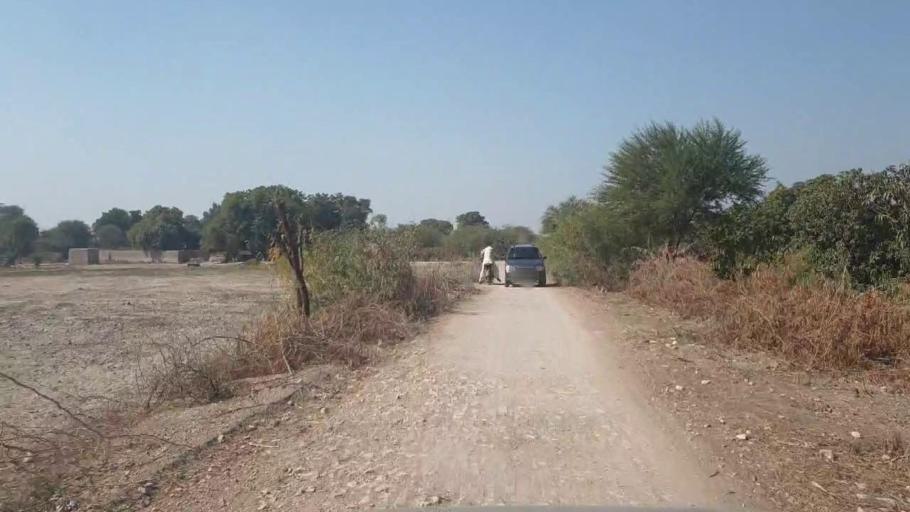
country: PK
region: Sindh
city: Chambar
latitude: 25.2465
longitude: 68.8261
